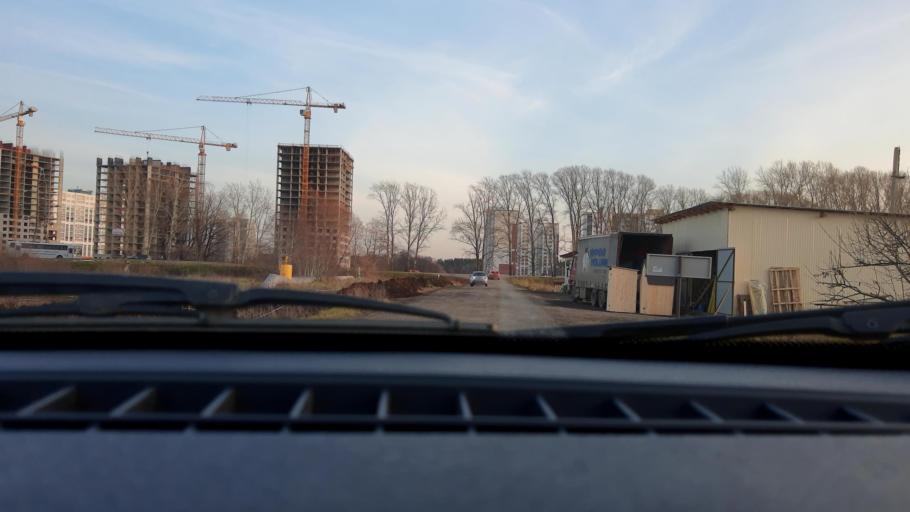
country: RU
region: Bashkortostan
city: Mikhaylovka
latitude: 54.7945
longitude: 55.8409
